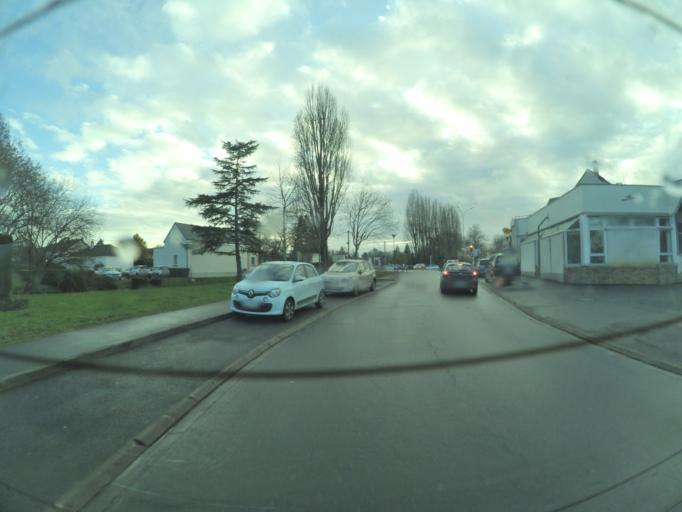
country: FR
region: Pays de la Loire
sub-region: Departement de la Sarthe
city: La Milesse
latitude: 48.0640
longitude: 0.1371
